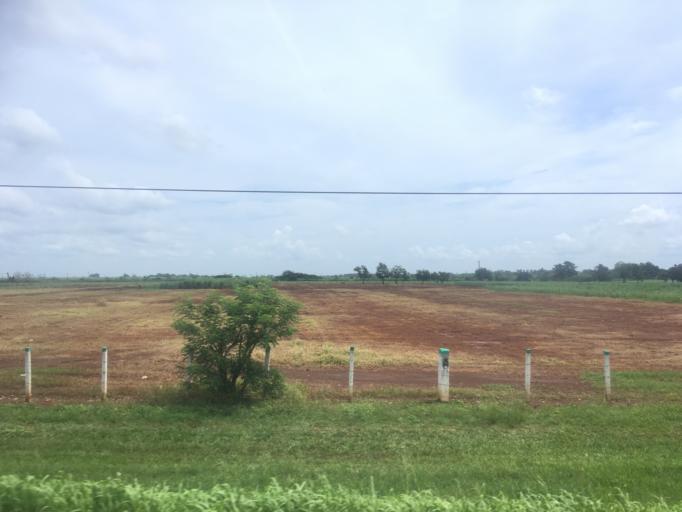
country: CU
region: Matanzas
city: Jovellanos
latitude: 22.7968
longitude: -81.1466
